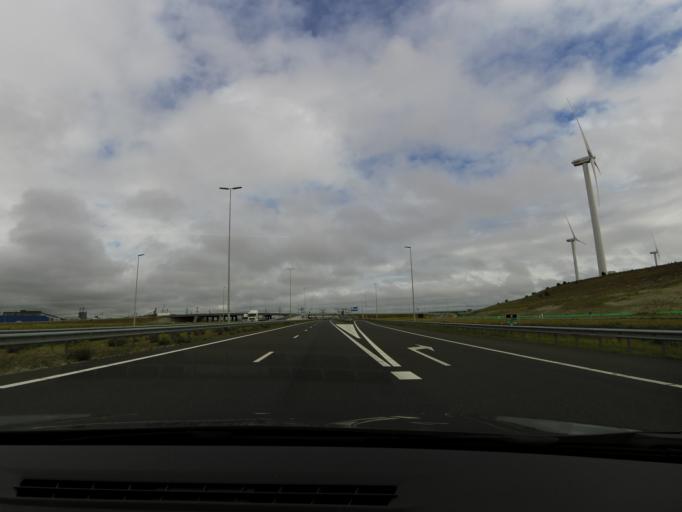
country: NL
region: South Holland
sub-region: Gemeente Goeree-Overflakkee
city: Goedereede
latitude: 51.9338
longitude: 4.0132
